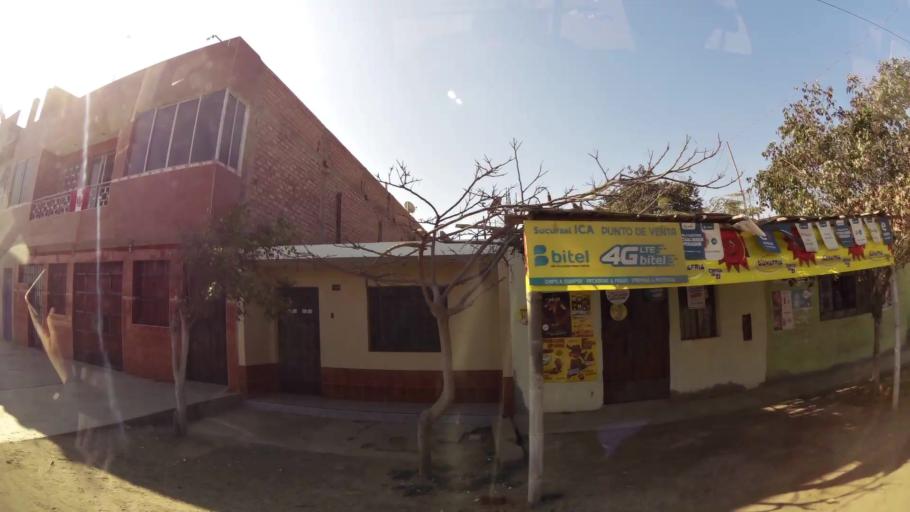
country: PE
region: Ica
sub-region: Provincia de Chincha
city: Chincha Alta
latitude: -13.3988
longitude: -76.1248
